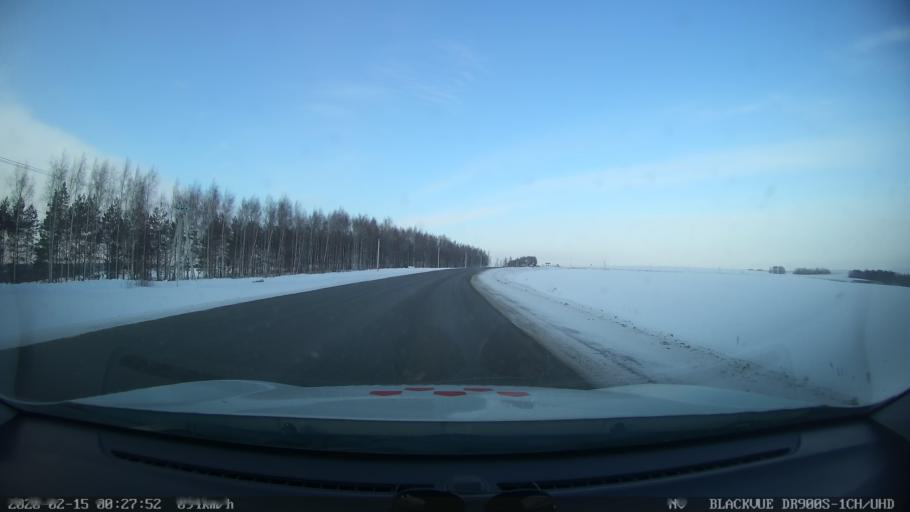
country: RU
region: Tatarstan
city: Verkhniy Uslon
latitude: 55.6346
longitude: 48.8710
